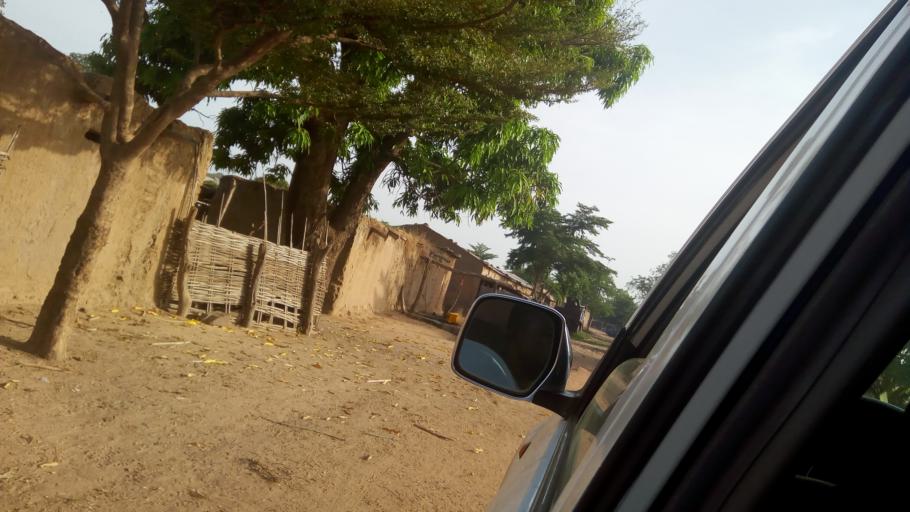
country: ML
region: Kayes
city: Kita
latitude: 13.1347
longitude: -8.8307
